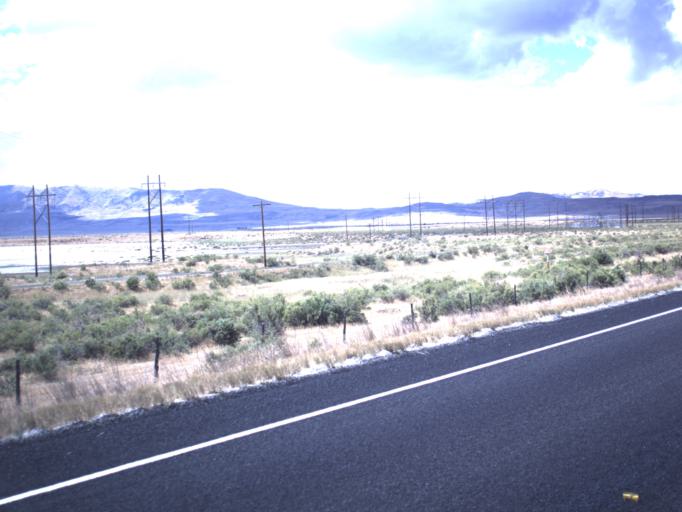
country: US
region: Utah
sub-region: Box Elder County
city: Tremonton
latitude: 41.6175
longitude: -112.3817
